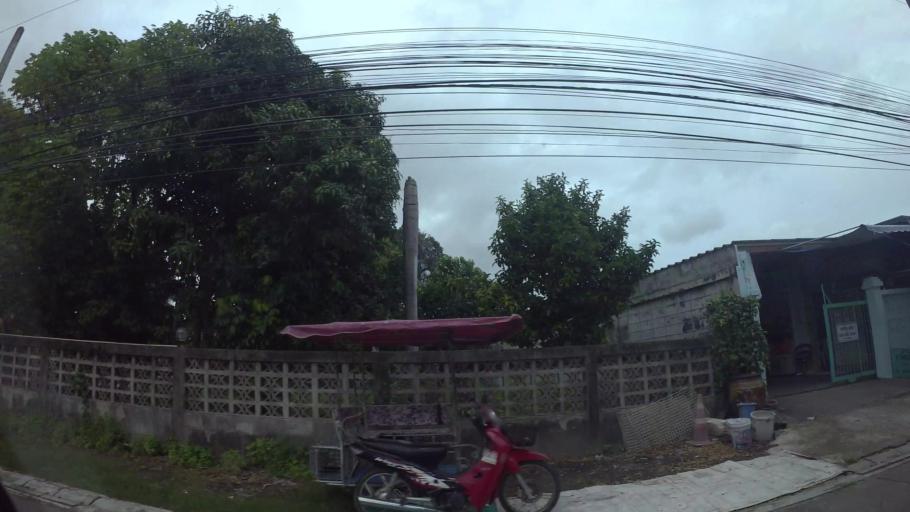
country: TH
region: Rayong
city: Rayong
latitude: 12.6711
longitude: 101.2810
